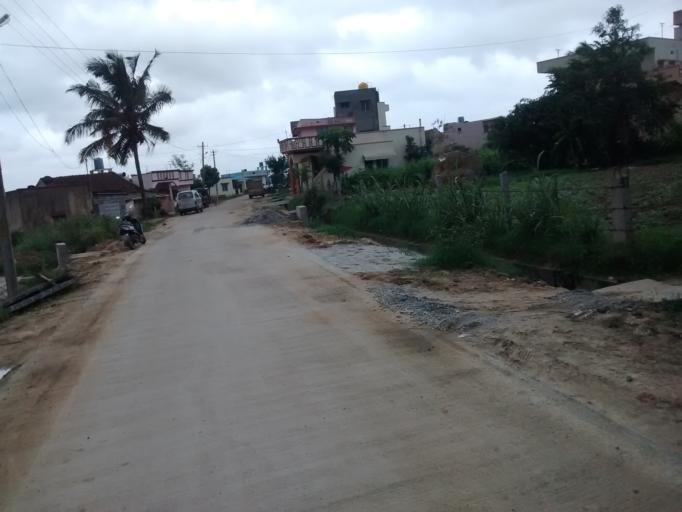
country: IN
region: Karnataka
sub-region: Hassan
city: Hassan
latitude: 12.9542
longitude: 76.1297
